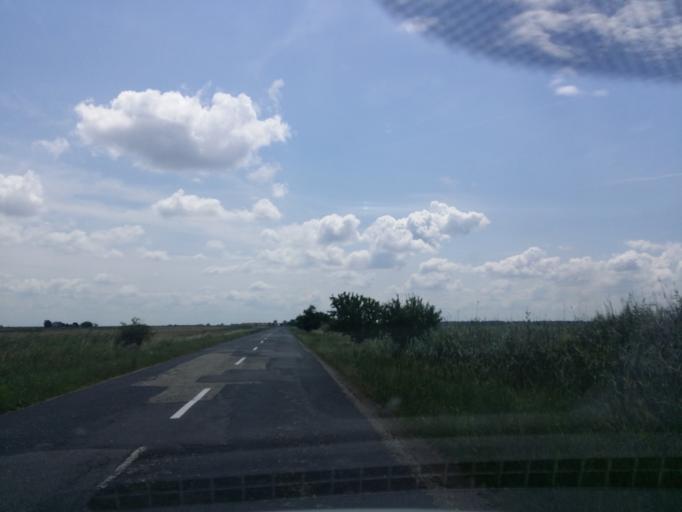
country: HU
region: Hajdu-Bihar
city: Hortobagy
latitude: 47.5975
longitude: 21.0768
